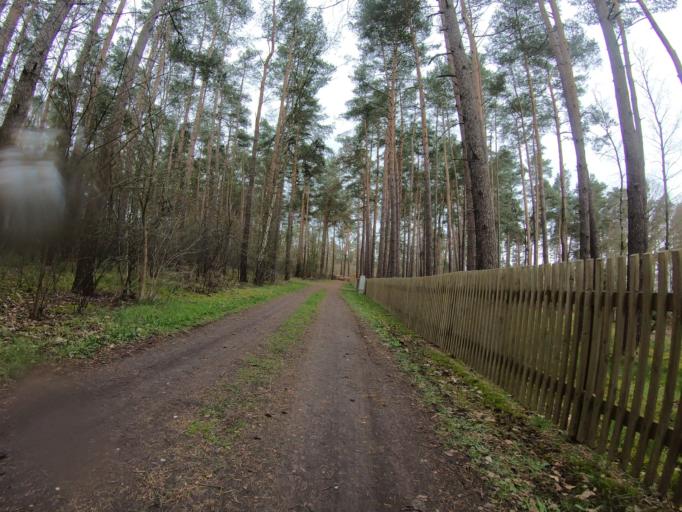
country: DE
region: Lower Saxony
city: Wagenhoff
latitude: 52.4889
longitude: 10.4811
